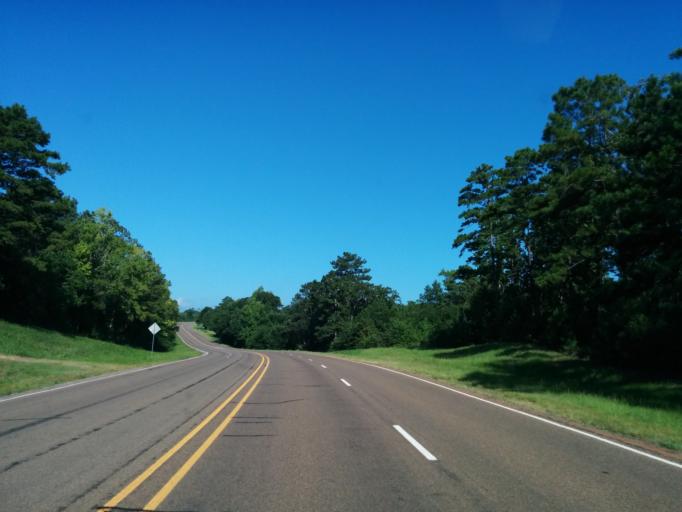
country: US
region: Texas
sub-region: Sabine County
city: Milam
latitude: 31.4313
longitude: -93.8186
